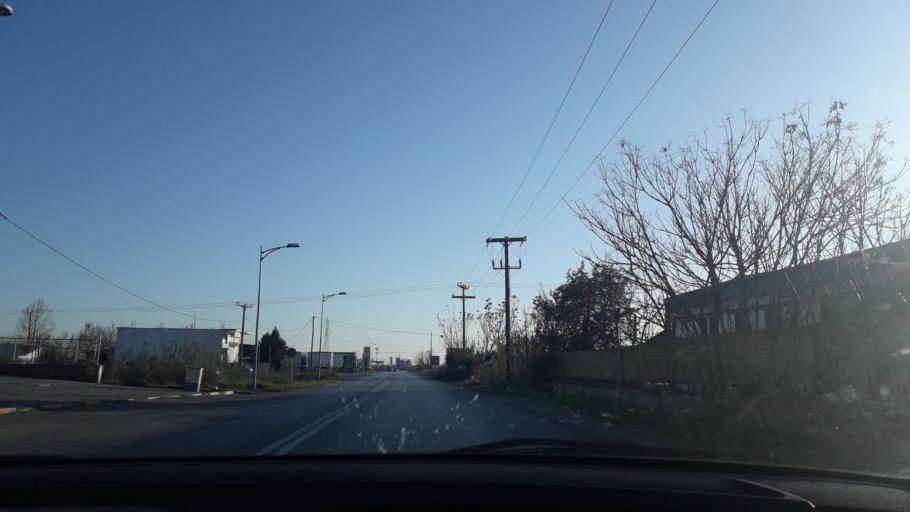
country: GR
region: Central Macedonia
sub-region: Nomos Pellis
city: Giannitsa
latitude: 40.7812
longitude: 22.4048
